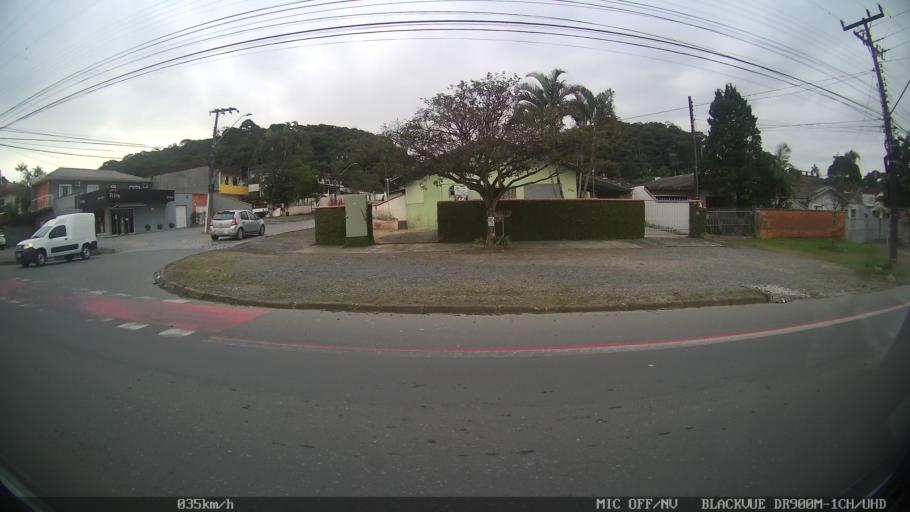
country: BR
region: Santa Catarina
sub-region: Joinville
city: Joinville
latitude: -26.2845
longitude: -48.8822
